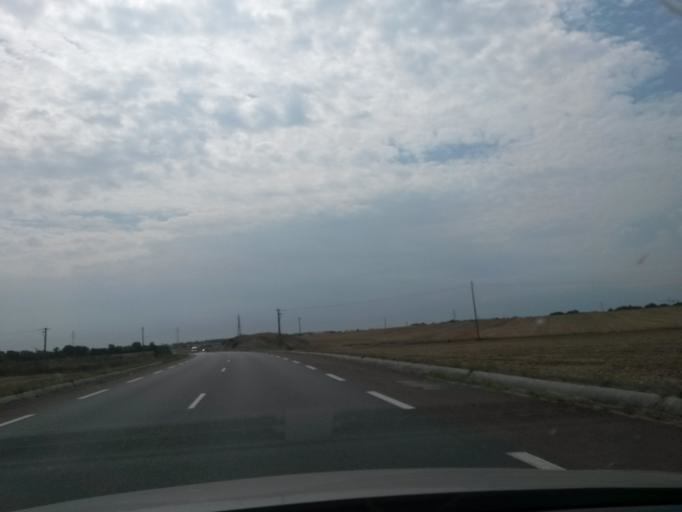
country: FR
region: Poitou-Charentes
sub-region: Departement de la Charente-Maritime
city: Saint-Xandre
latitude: 46.2122
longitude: -1.0908
